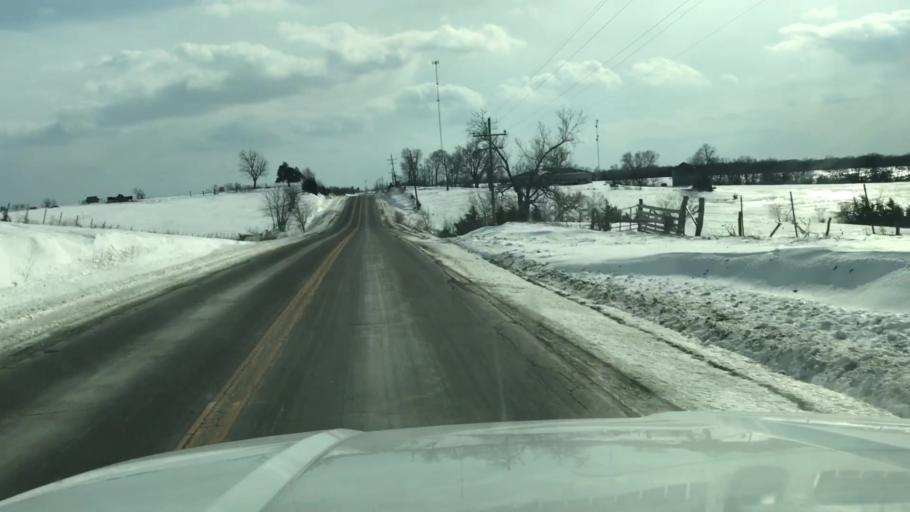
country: US
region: Missouri
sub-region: Gentry County
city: Stanberry
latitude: 40.3765
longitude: -94.6472
